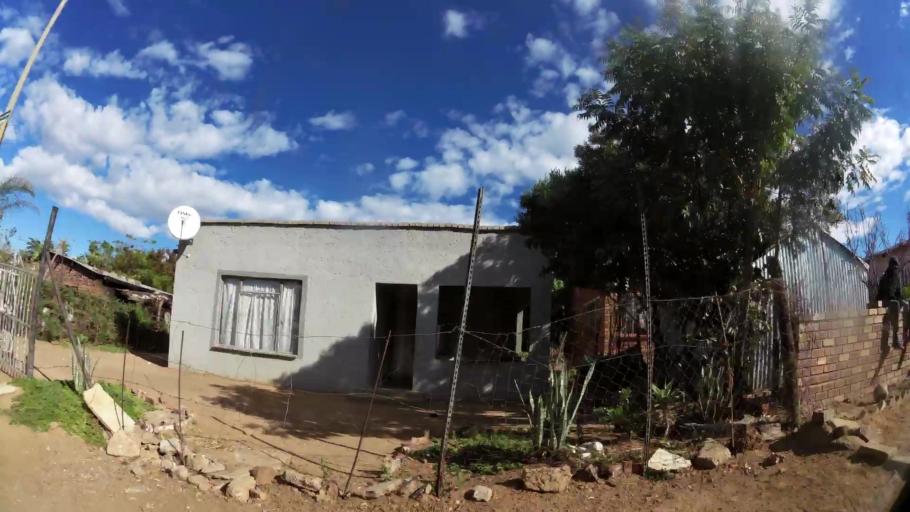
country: ZA
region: Limpopo
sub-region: Waterberg District Municipality
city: Warmbaths
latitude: -24.8792
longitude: 28.2724
